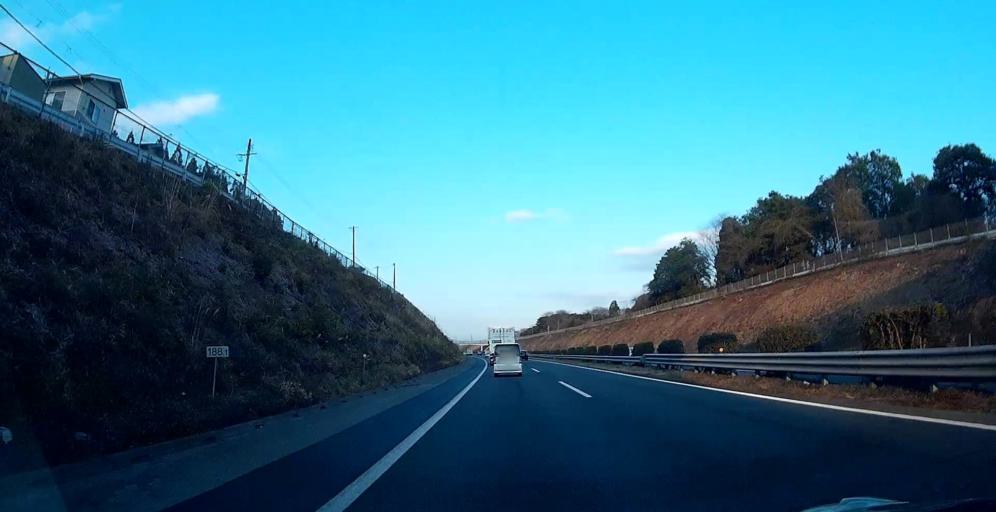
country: JP
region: Kumamoto
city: Uto
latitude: 32.6983
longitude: 130.7486
